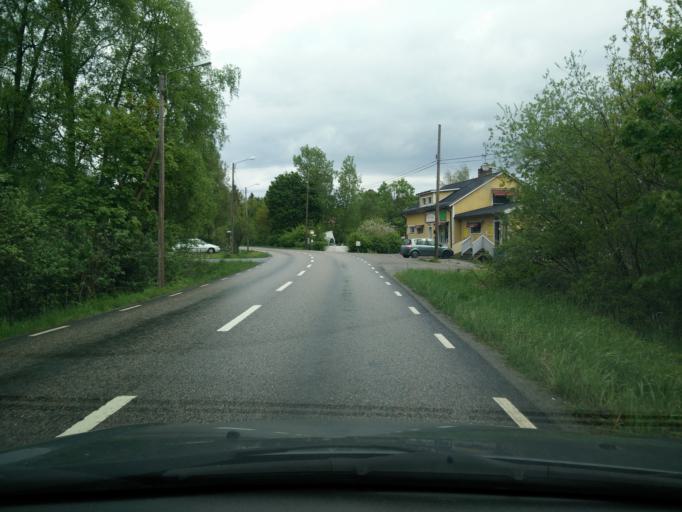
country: SE
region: Stockholm
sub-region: Norrtalje Kommun
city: Bjorko
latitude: 59.8099
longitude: 18.8938
